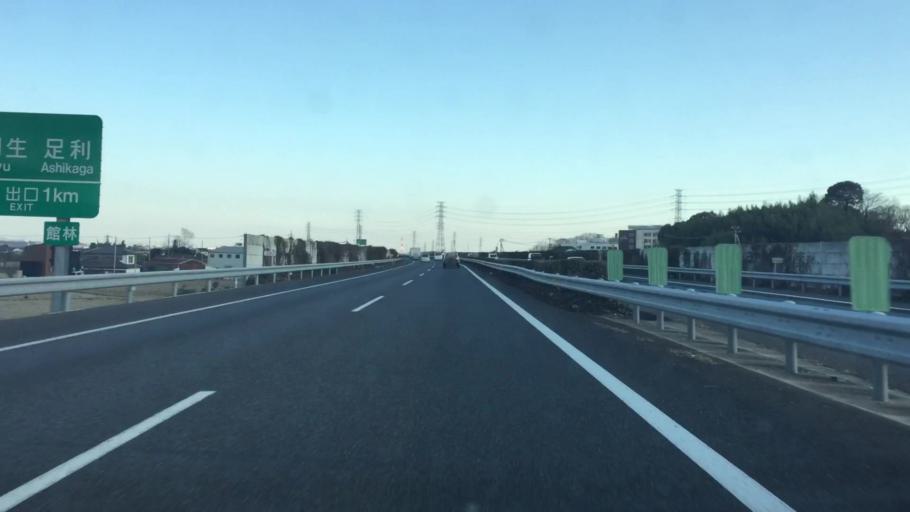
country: JP
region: Gunma
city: Ota
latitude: 36.3323
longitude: 139.3762
